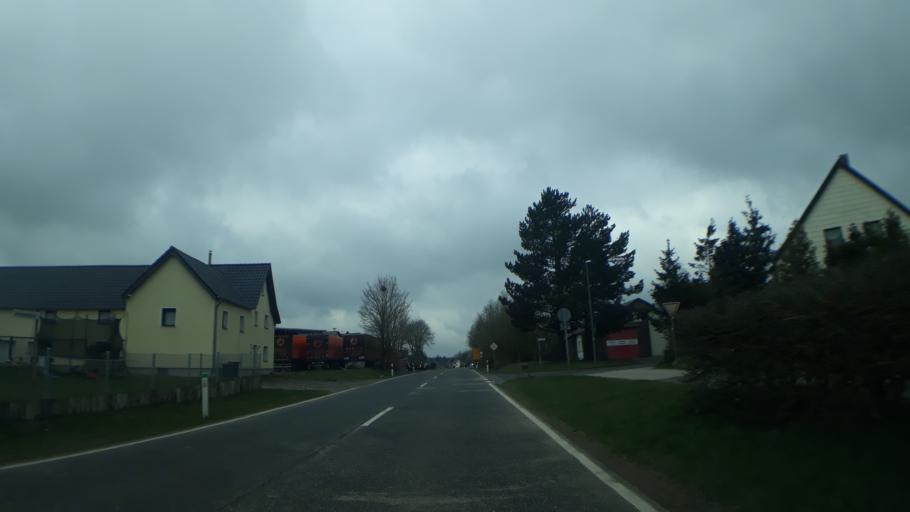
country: DE
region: North Rhine-Westphalia
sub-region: Regierungsbezirk Koln
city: Schleiden
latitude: 50.5544
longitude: 6.4586
